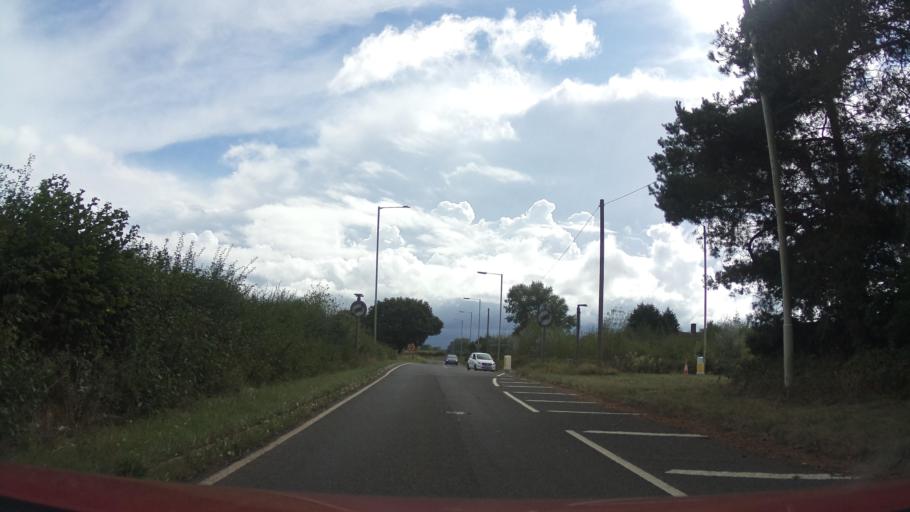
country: GB
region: England
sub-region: Telford and Wrekin
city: Madeley
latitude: 52.6407
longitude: -2.4120
